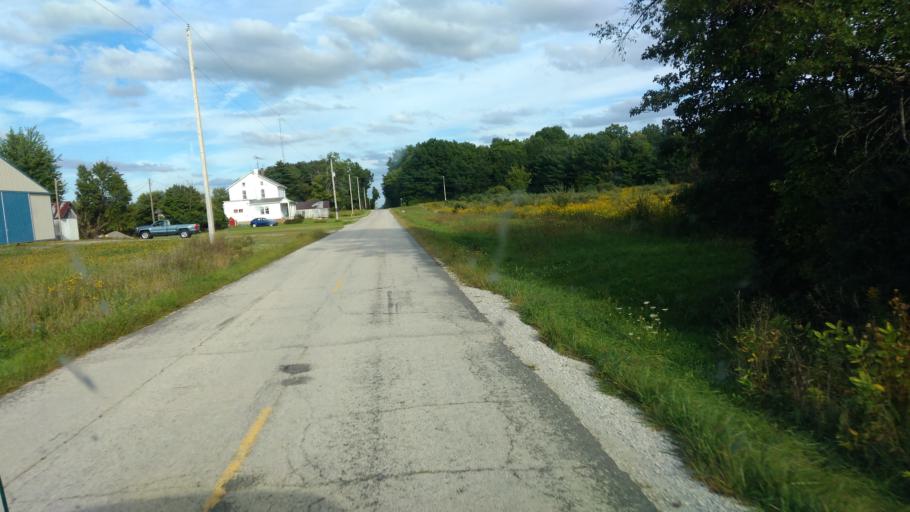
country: US
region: Ohio
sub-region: Crawford County
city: Bucyrus
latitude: 40.9212
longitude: -83.0004
